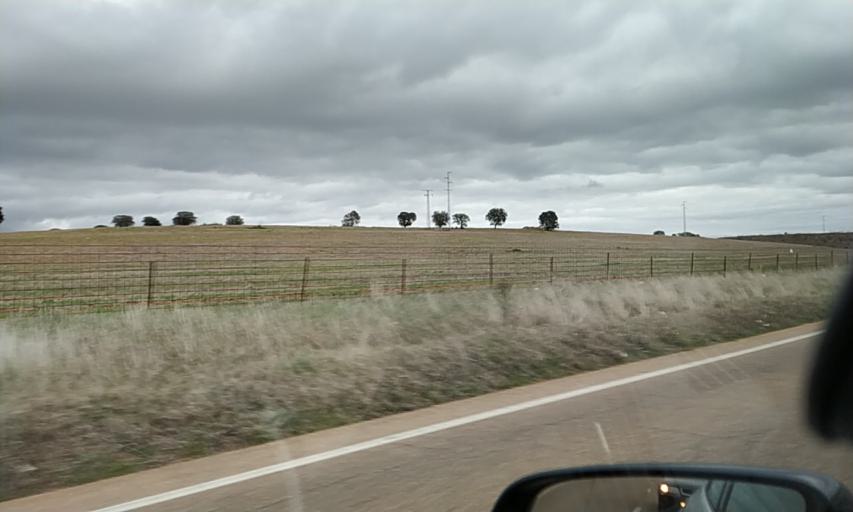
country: ES
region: Extremadura
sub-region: Provincia de Badajoz
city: Badajoz
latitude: 38.9232
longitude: -7.0077
